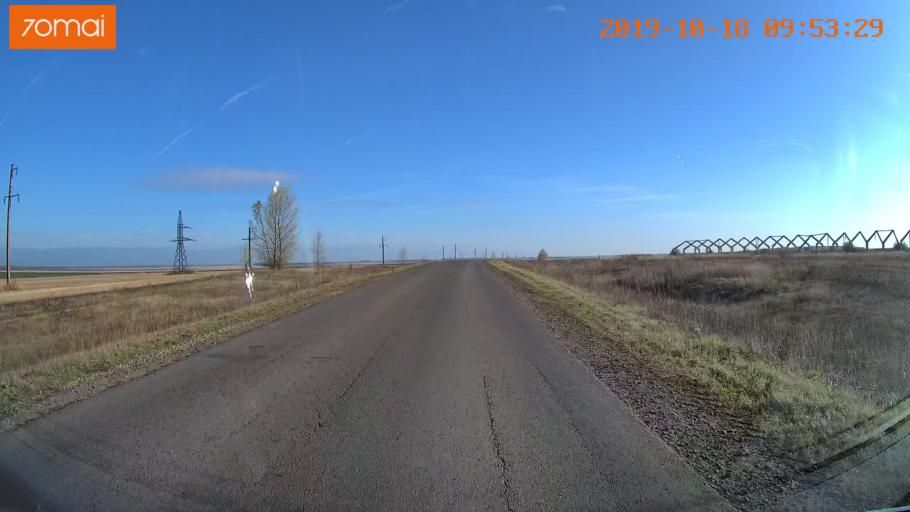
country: RU
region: Tula
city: Kazachka
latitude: 53.3613
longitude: 38.3298
